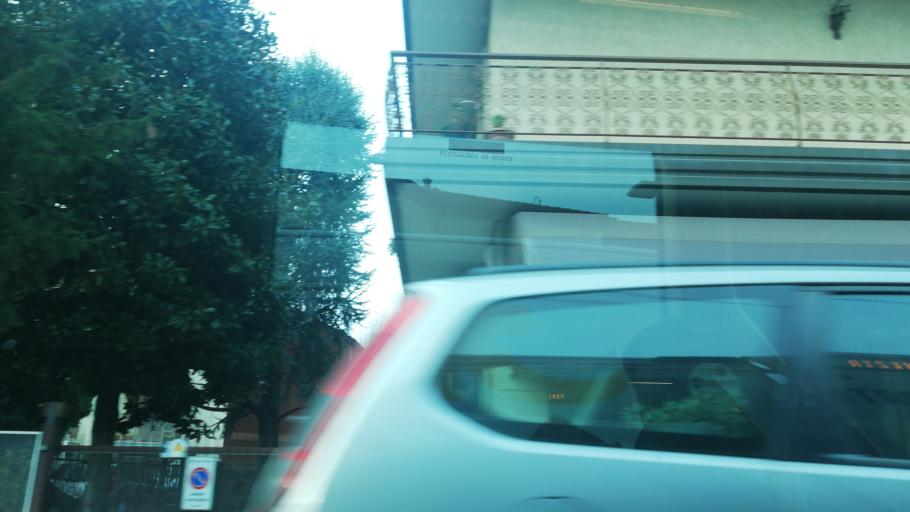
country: IT
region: Veneto
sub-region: Provincia di Venezia
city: Mestre
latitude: 45.5037
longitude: 12.2552
